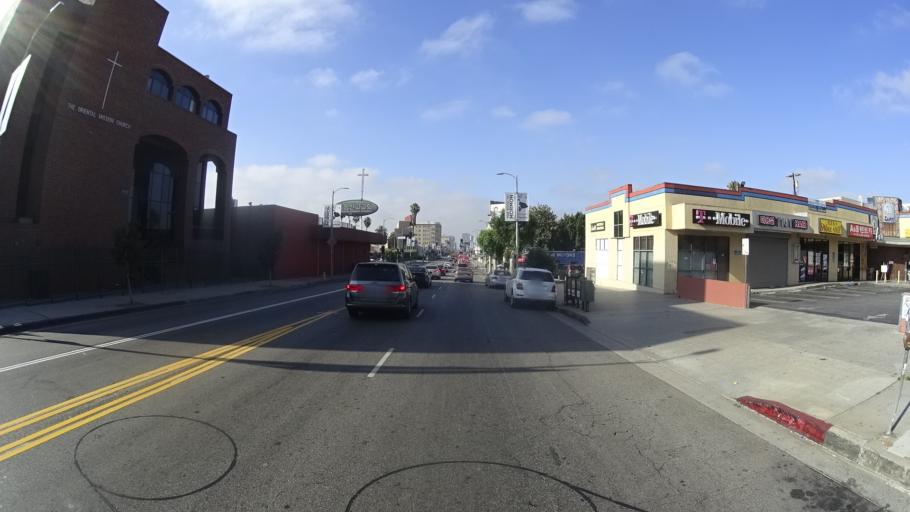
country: US
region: California
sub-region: Los Angeles County
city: Hollywood
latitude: 34.0792
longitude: -118.3092
